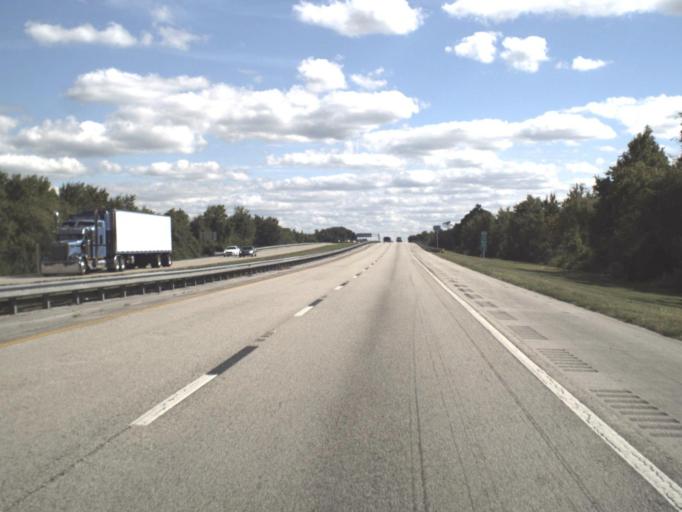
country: US
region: Florida
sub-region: Indian River County
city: Fellsmere
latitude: 27.5944
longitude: -80.8175
